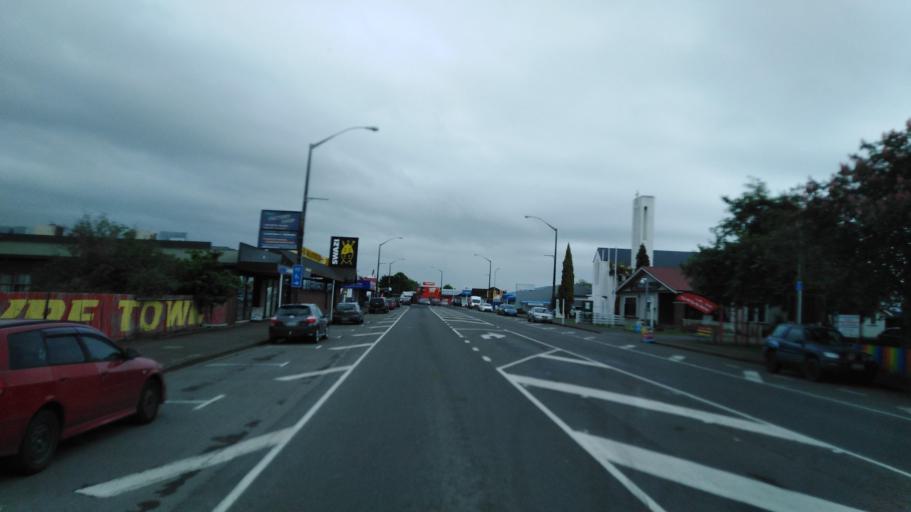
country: NZ
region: Manawatu-Wanganui
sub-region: Horowhenua District
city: Levin
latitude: -40.6261
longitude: 175.2822
